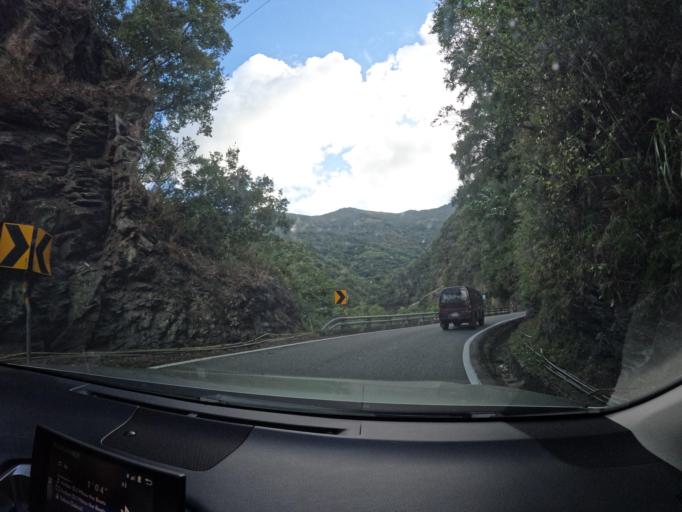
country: TW
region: Taiwan
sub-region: Taitung
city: Taitung
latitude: 23.1618
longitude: 121.0510
